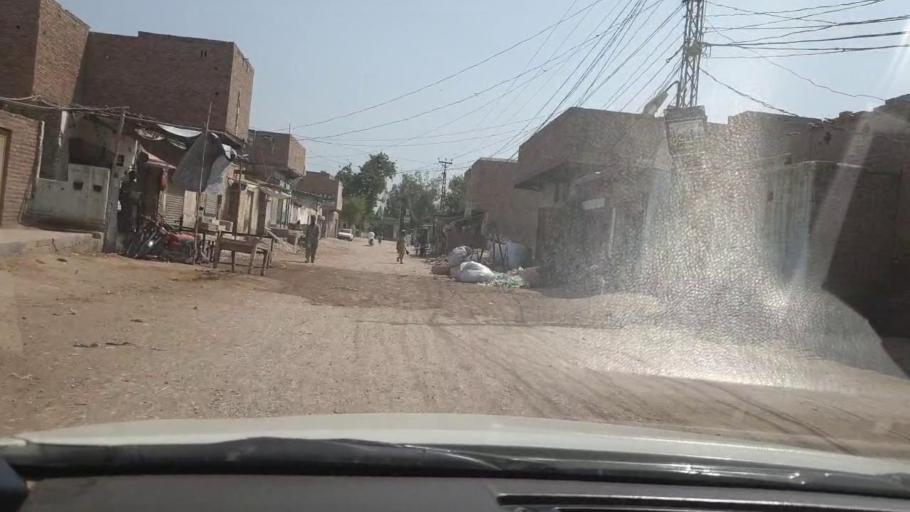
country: PK
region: Sindh
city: Shikarpur
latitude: 27.9469
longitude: 68.6300
